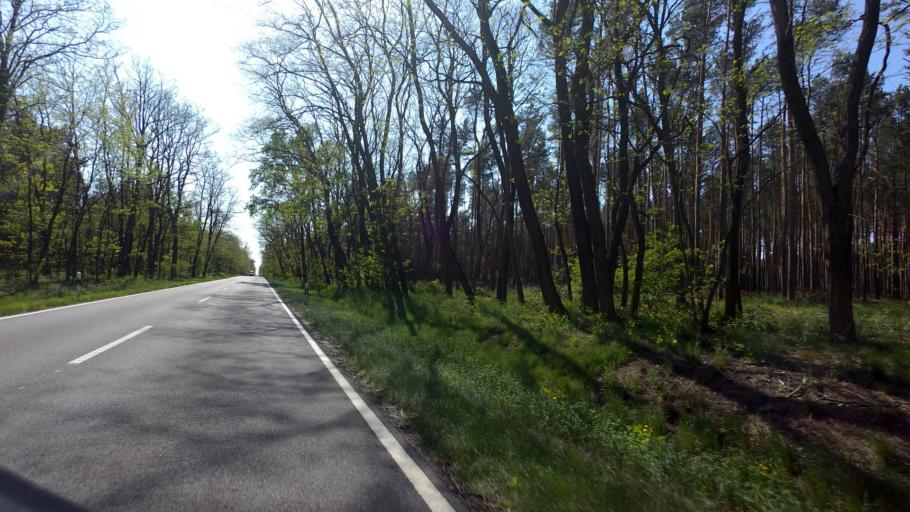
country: DE
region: Brandenburg
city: Tauche
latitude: 52.0473
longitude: 14.1191
